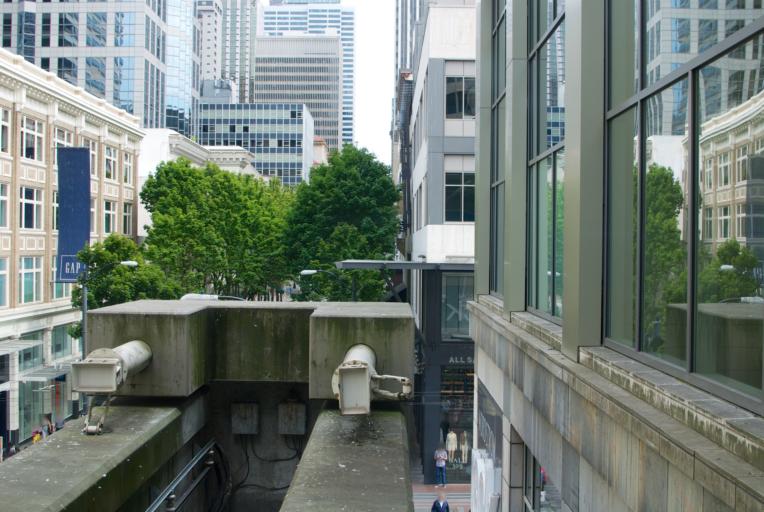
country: US
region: Washington
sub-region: King County
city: Seattle
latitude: 47.6123
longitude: -122.3368
